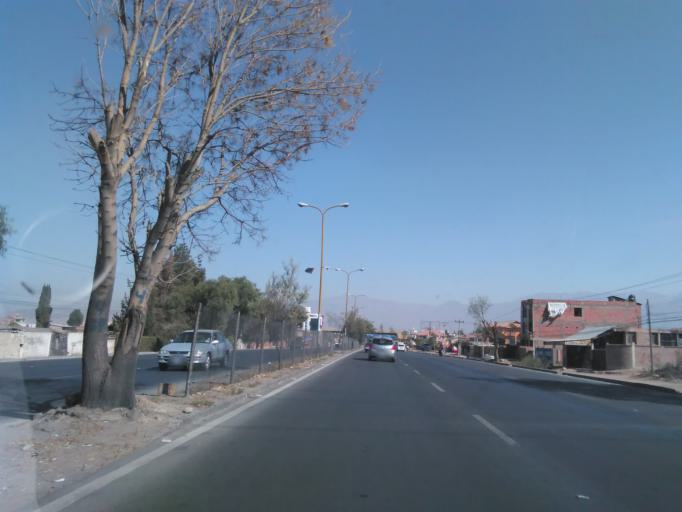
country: BO
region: Cochabamba
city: Cochabamba
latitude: -17.3909
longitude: -66.2461
